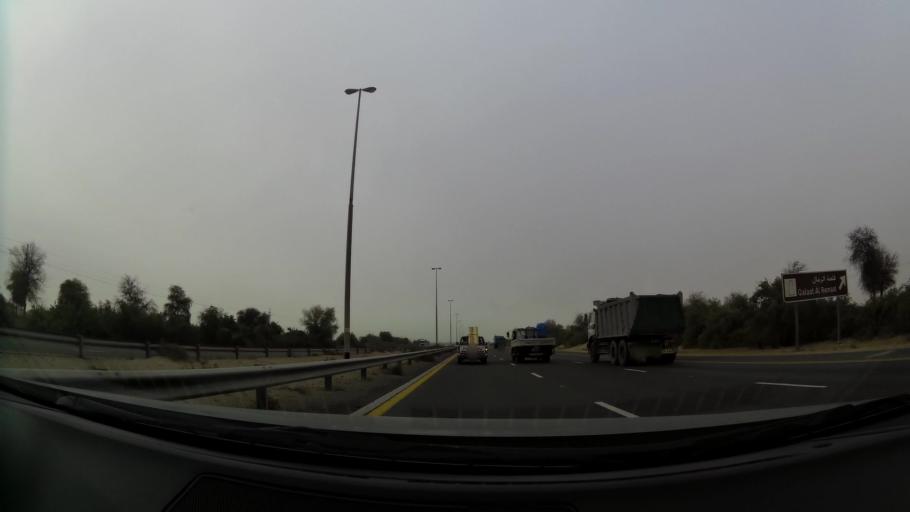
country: AE
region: Dubai
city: Dubai
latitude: 25.0659
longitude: 55.4103
